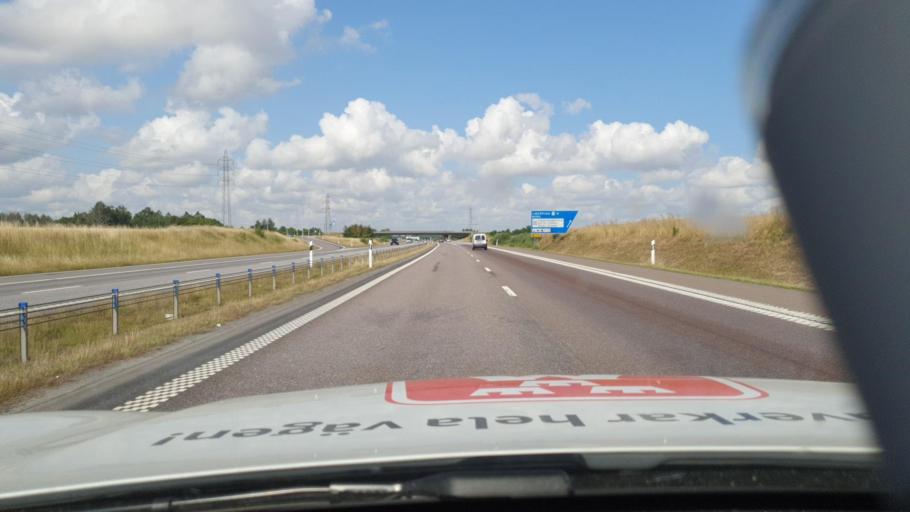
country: SE
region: OEstergoetland
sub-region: Linkopings Kommun
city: Linkoping
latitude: 58.4381
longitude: 15.5905
